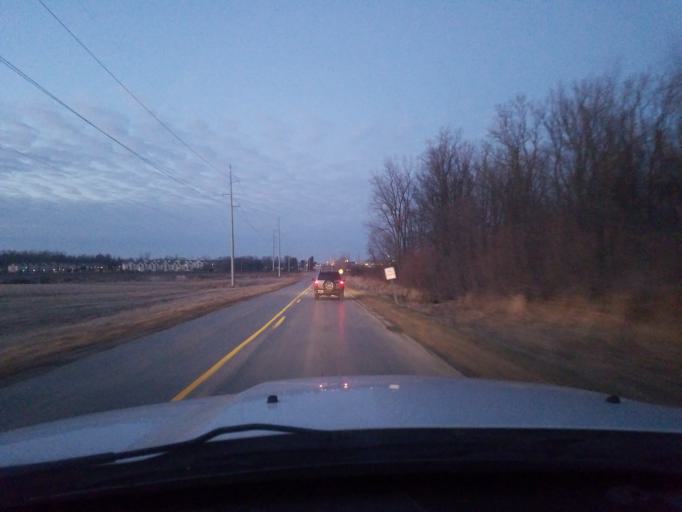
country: US
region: Indiana
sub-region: Huntington County
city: Roanoke
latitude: 41.0189
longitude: -85.2555
